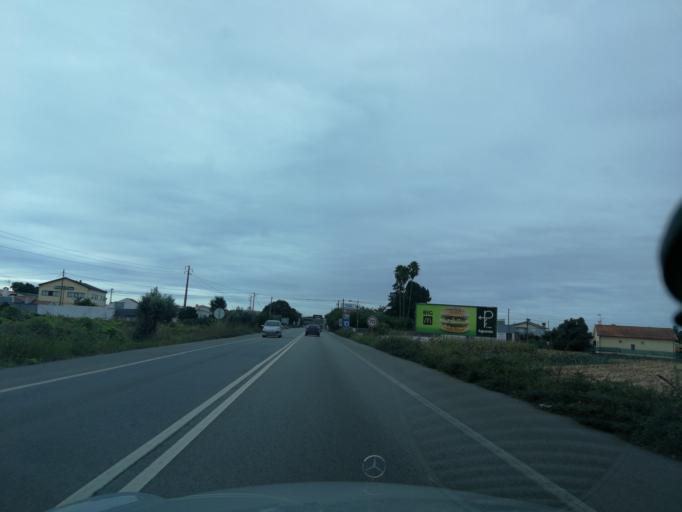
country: PT
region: Aveiro
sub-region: Agueda
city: Valongo
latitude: 40.6157
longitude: -8.4636
